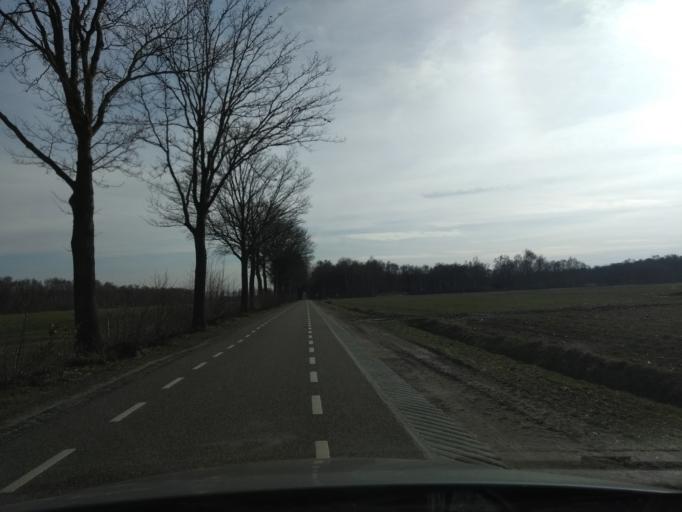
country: NL
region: Overijssel
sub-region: Gemeente Twenterand
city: Westerhaar-Vriezenveensewijk
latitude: 52.4492
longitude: 6.6542
